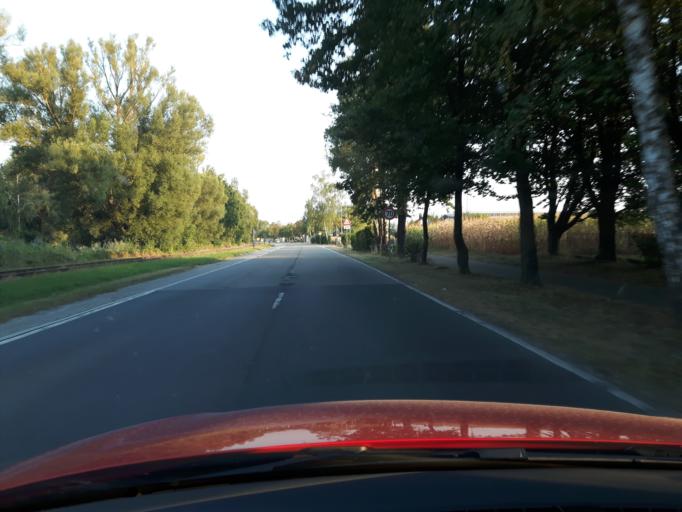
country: DE
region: Rheinland-Pfalz
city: Hagenbach
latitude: 49.0155
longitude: 8.2548
